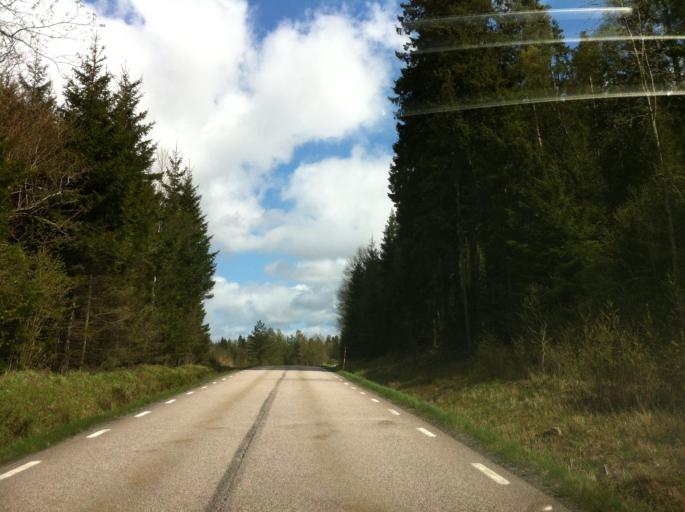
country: SE
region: Vaestra Goetaland
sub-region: Alingsas Kommun
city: Ingared
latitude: 57.8463
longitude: 12.5530
